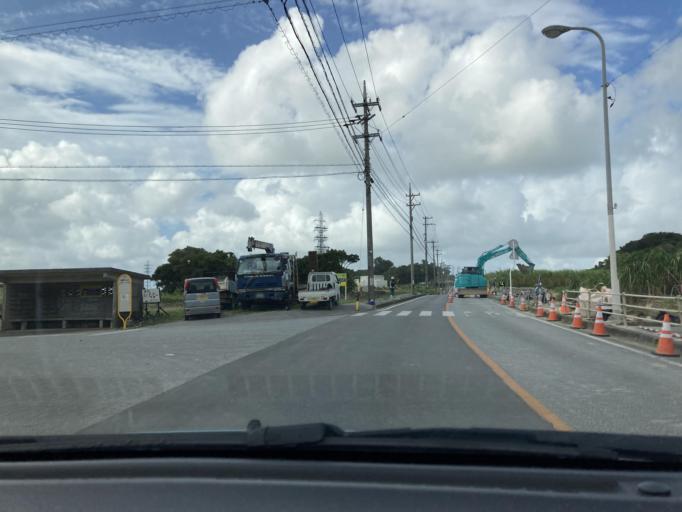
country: JP
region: Okinawa
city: Itoman
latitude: 26.1057
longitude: 127.6951
